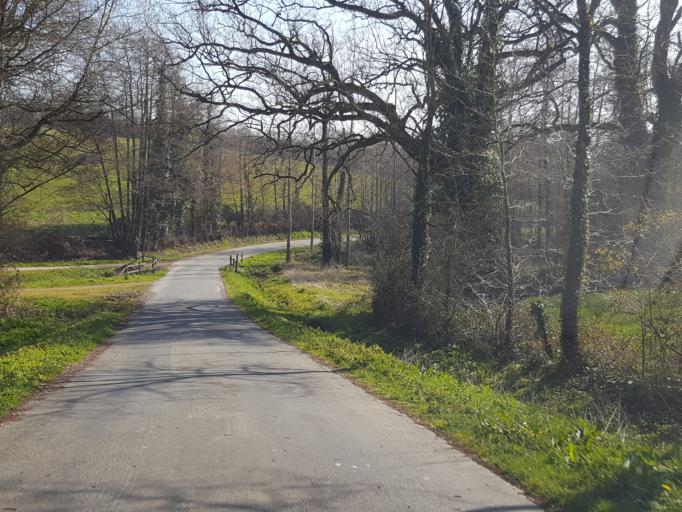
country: FR
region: Pays de la Loire
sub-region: Departement de la Vendee
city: La Chaize-le-Vicomte
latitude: 46.6588
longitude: -1.3063
